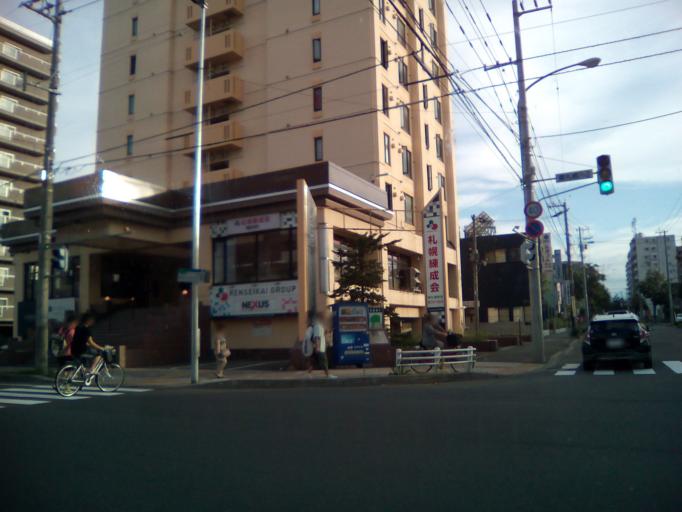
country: JP
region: Hokkaido
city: Sapporo
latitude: 43.0523
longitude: 141.3842
